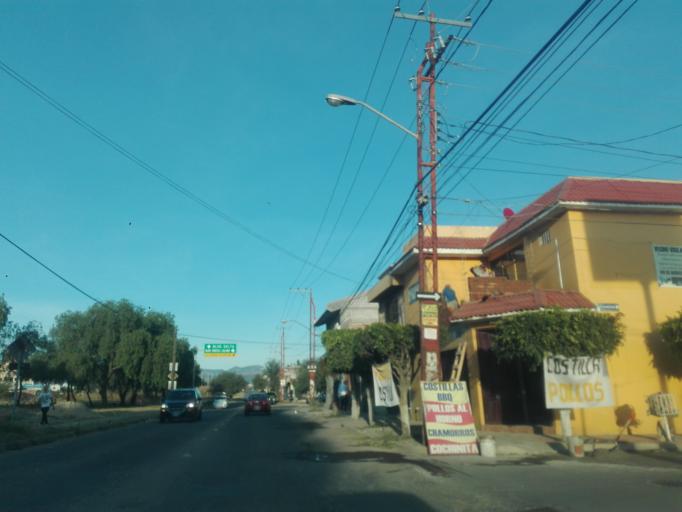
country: MX
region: Guanajuato
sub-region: Leon
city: San Jose de Duran (Los Troncoso)
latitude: 21.0865
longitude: -101.6478
